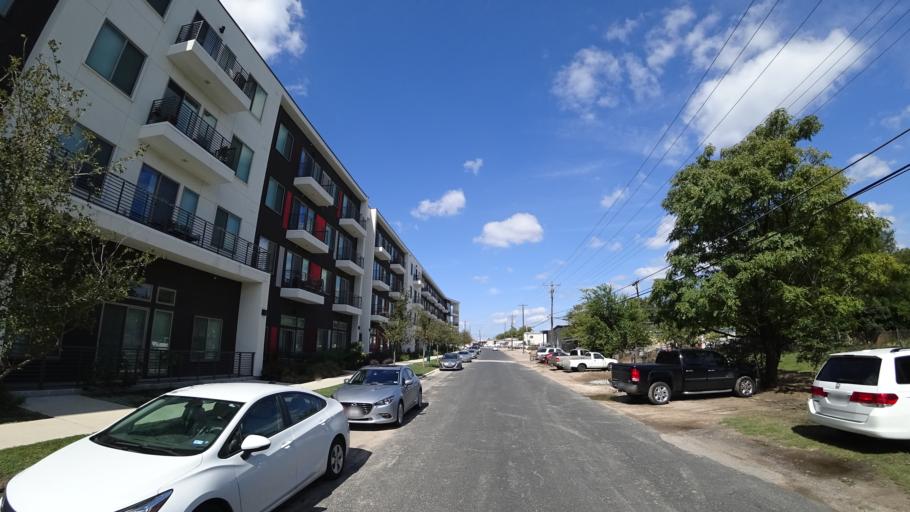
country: US
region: Texas
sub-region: Travis County
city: Austin
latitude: 30.3416
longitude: -97.7376
